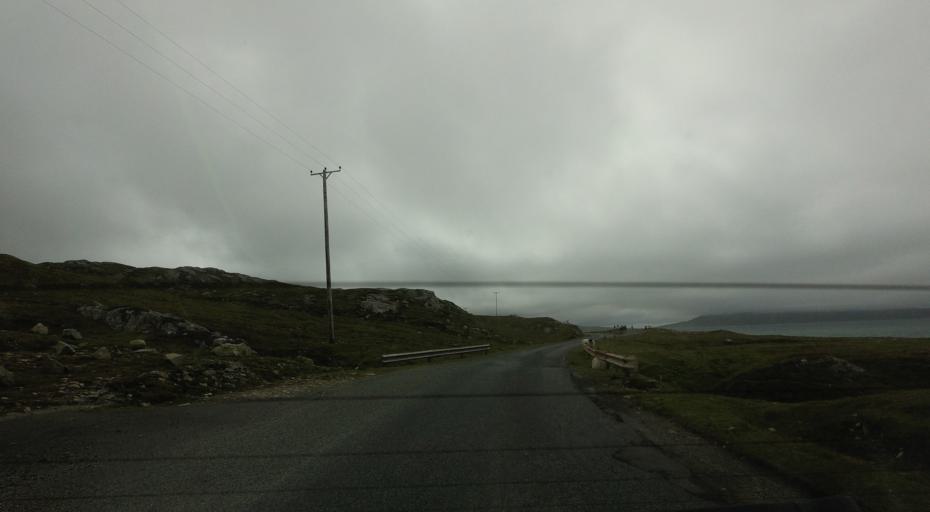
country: GB
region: Scotland
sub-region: Eilean Siar
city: Harris
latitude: 57.8556
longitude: -6.9986
